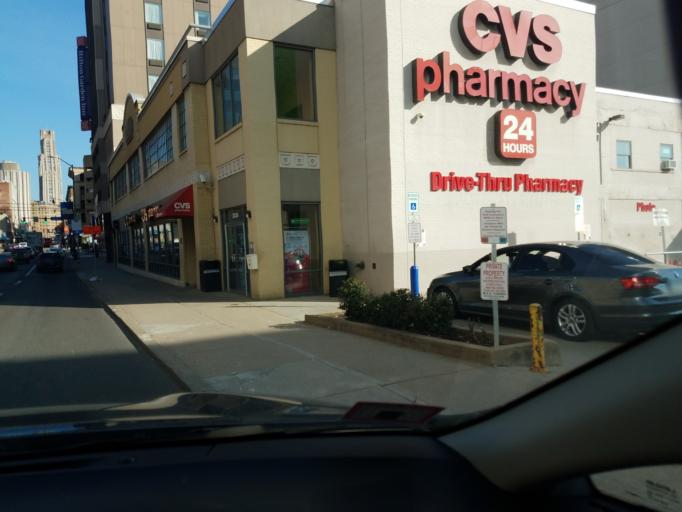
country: US
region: Pennsylvania
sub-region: Allegheny County
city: Bloomfield
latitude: 40.4392
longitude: -79.9602
